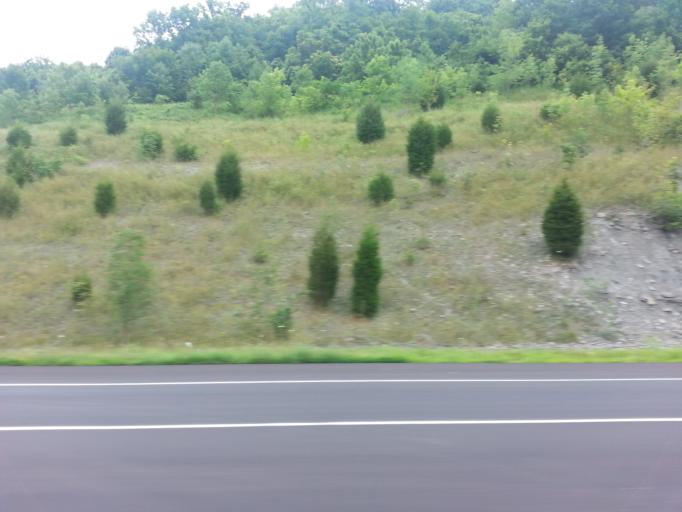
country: US
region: Ohio
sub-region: Brown County
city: Aberdeen
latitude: 38.6825
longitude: -83.7909
